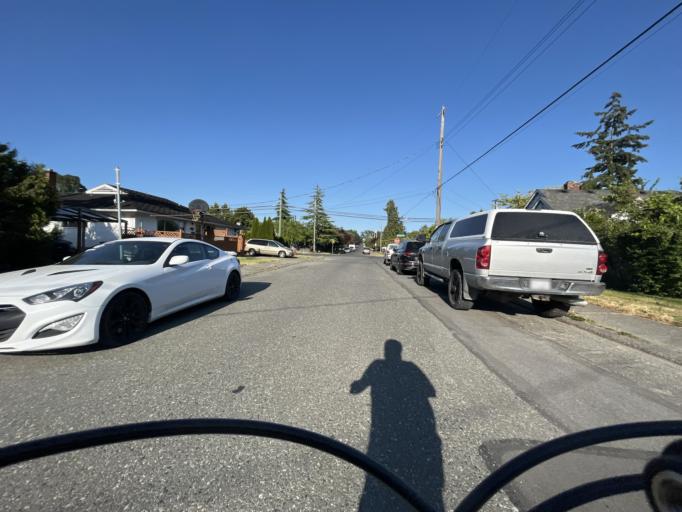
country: CA
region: British Columbia
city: Oak Bay
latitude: 48.4377
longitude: -123.3228
